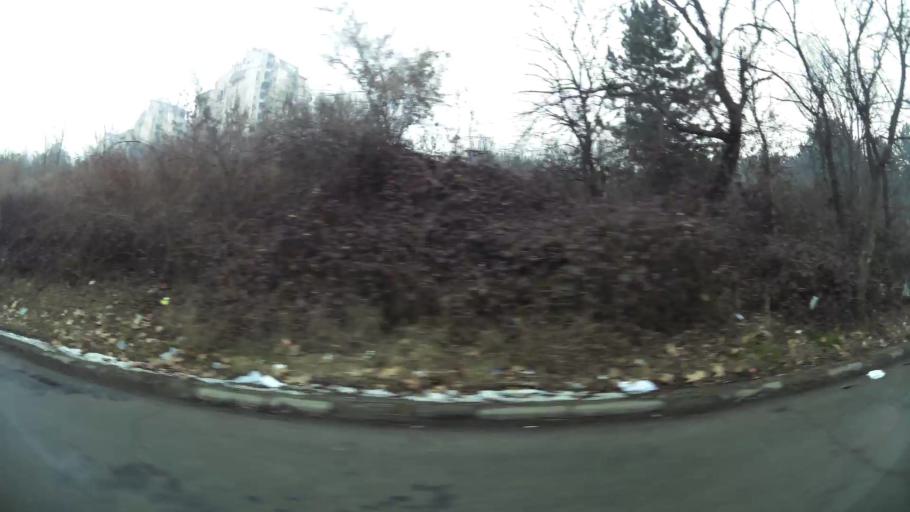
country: MK
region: Cair
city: Cair
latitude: 42.0080
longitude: 21.4618
